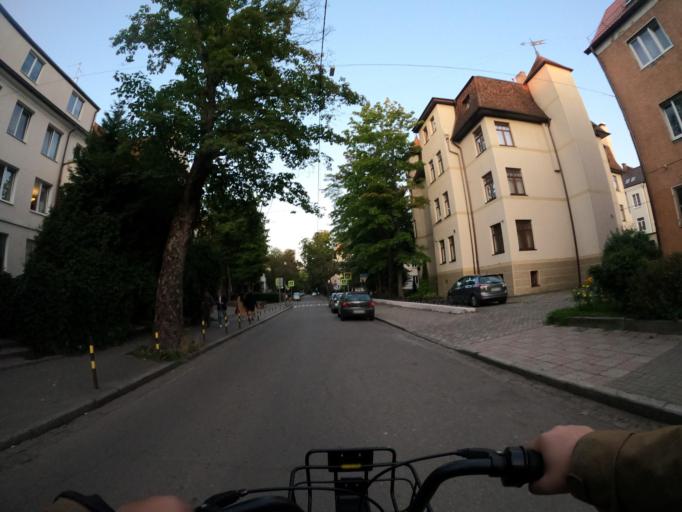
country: RU
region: Kaliningrad
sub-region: Gorod Kaliningrad
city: Kaliningrad
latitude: 54.7234
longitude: 20.4722
